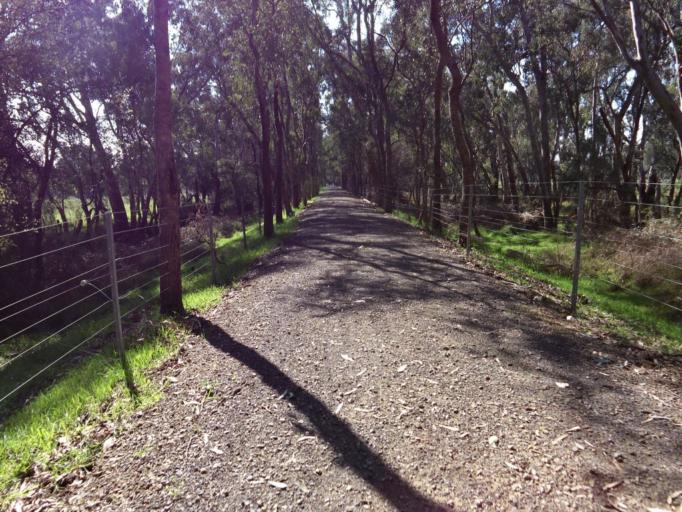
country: AU
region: Victoria
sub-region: Murrindindi
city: Alexandra
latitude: -37.1583
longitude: 145.5686
